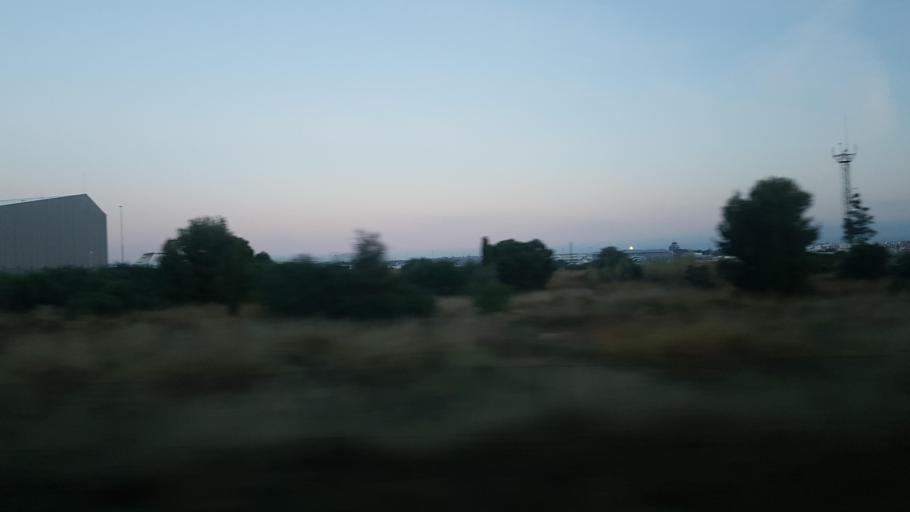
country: ES
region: Valencia
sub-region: Provincia de Valencia
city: Manises
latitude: 39.4792
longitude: -0.4716
